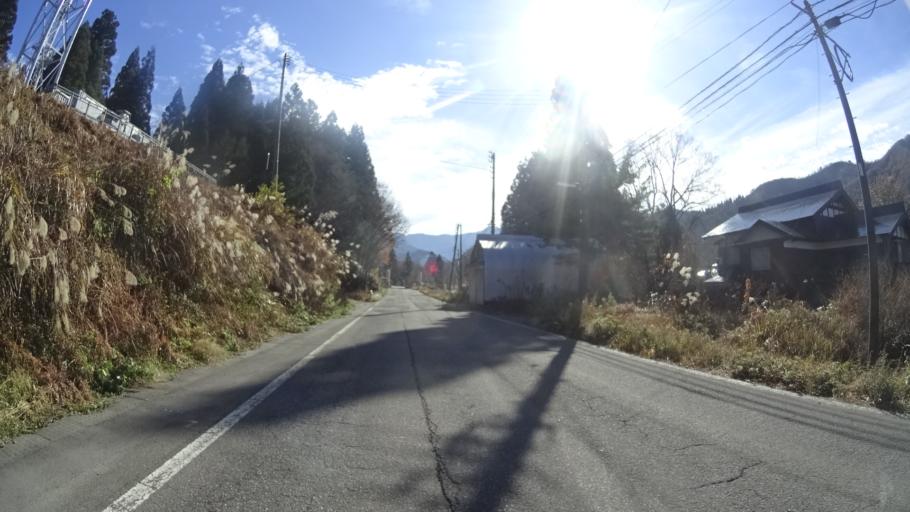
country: JP
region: Niigata
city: Muikamachi
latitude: 37.2009
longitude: 139.0757
